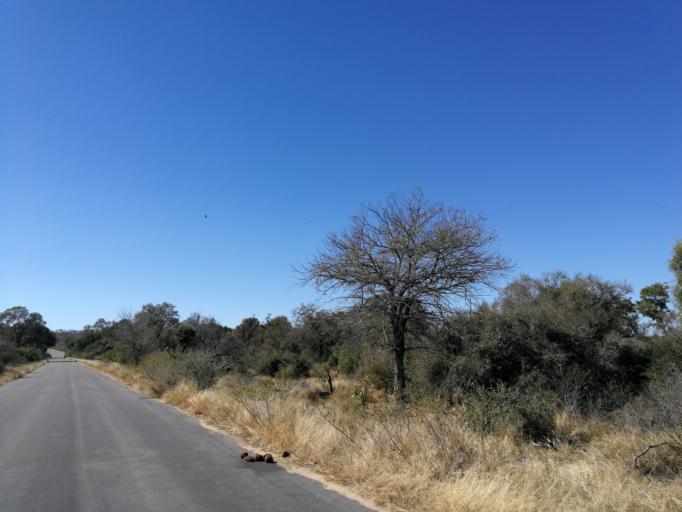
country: ZA
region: Limpopo
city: Thulamahashi
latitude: -24.9431
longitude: 31.6755
